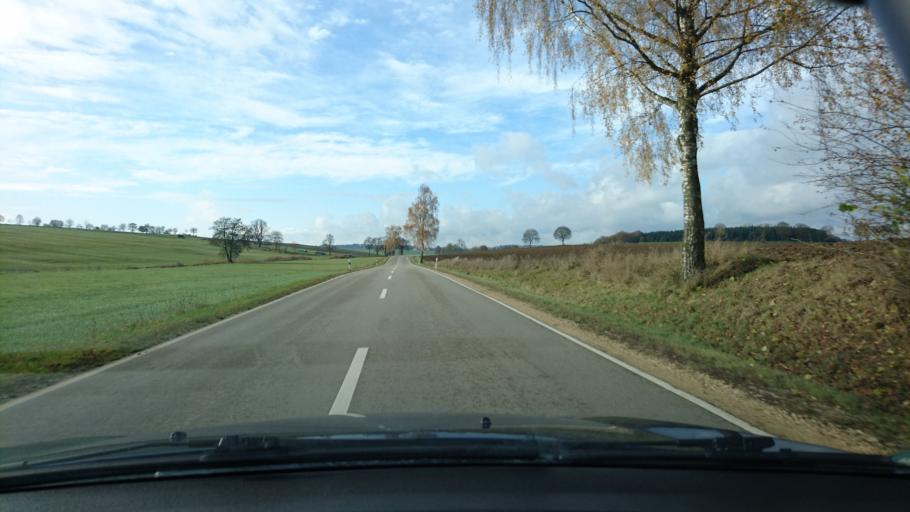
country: DE
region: Bavaria
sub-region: Swabia
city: Amerdingen
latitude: 48.7268
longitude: 10.5166
